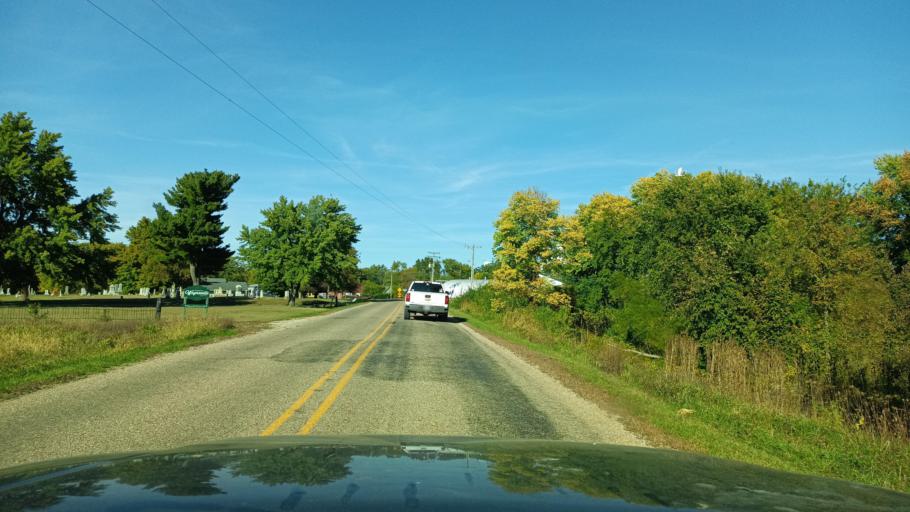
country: US
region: Illinois
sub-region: Logan County
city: Atlanta
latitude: 40.2369
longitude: -89.1290
